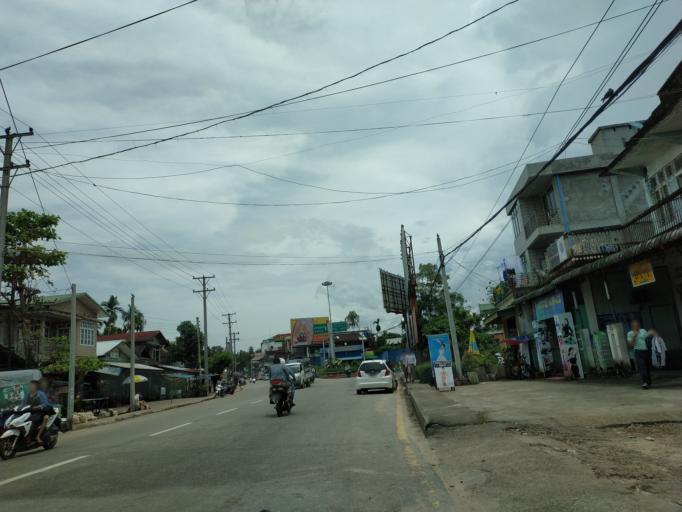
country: MM
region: Tanintharyi
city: Dawei
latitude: 14.0736
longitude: 98.2031
